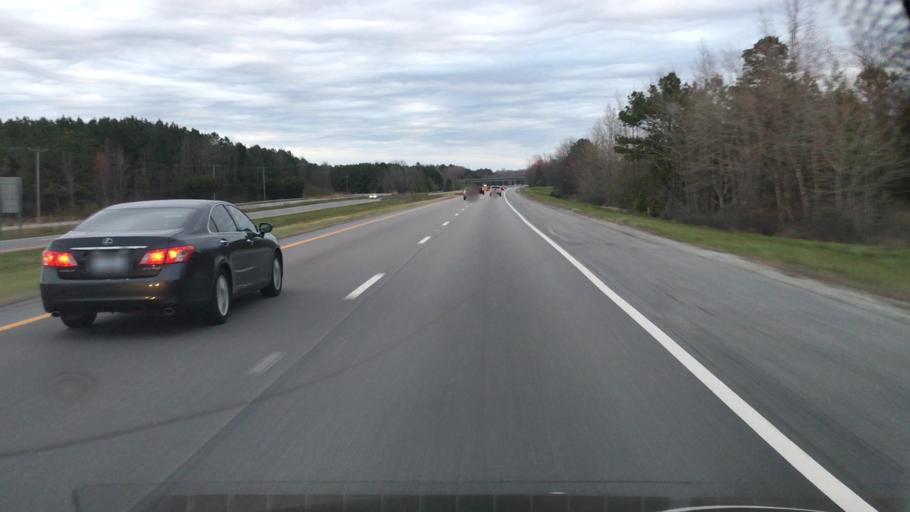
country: US
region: Virginia
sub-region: Sussex County
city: Sussex
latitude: 36.8687
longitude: -77.4094
